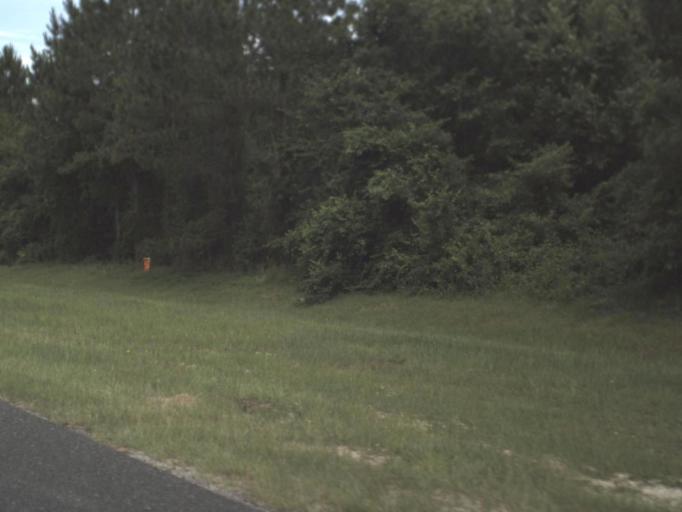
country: US
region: Florida
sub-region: Alachua County
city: Hawthorne
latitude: 29.5991
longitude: -82.1261
